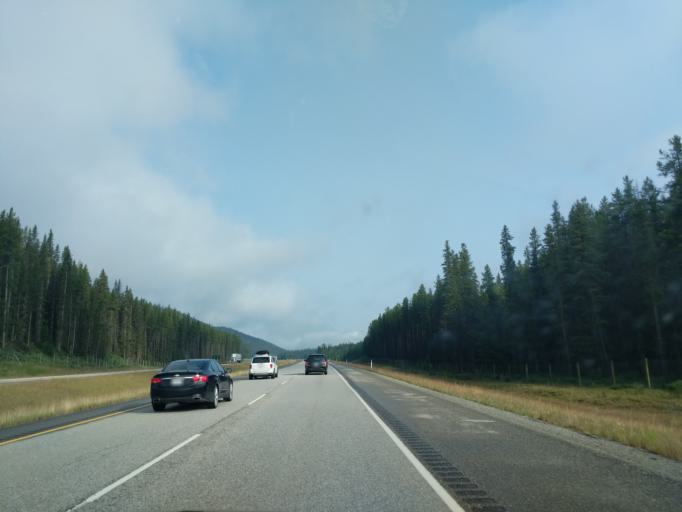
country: CA
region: Alberta
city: Lake Louise
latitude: 51.3190
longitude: -116.0363
